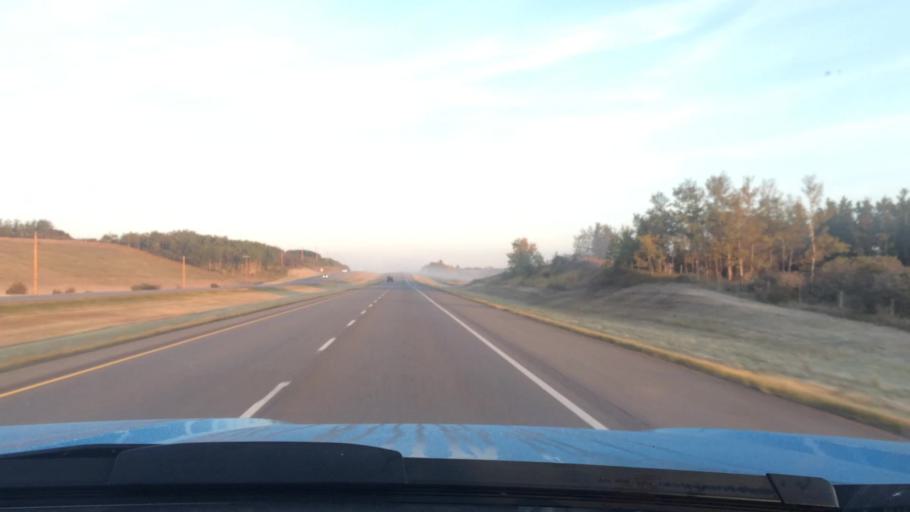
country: CA
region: Alberta
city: Cochrane
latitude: 51.0948
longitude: -114.5883
